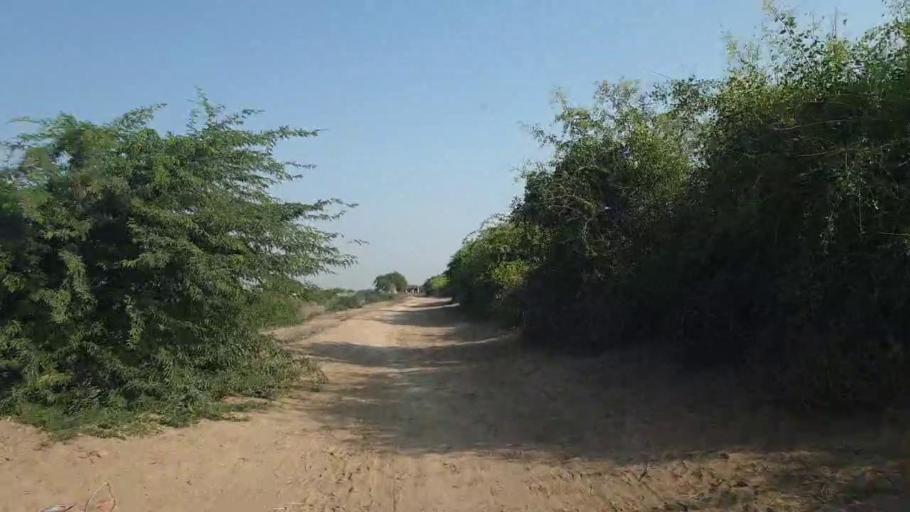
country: PK
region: Sindh
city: Badin
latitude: 24.4666
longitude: 68.7392
